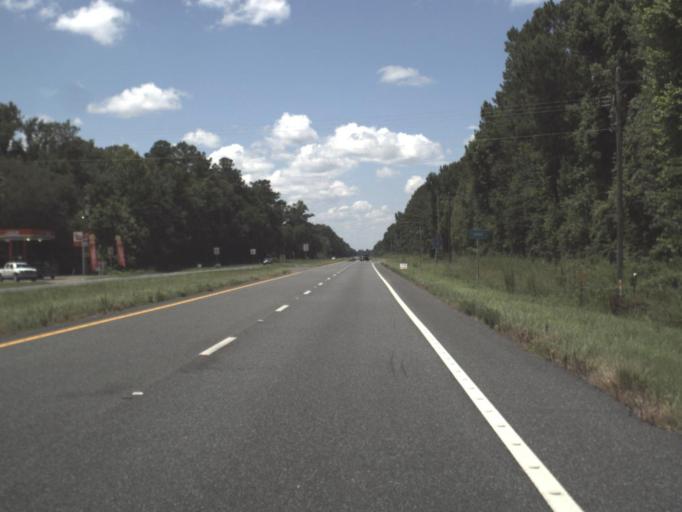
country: US
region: Florida
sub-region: Taylor County
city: Perry
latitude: 30.2995
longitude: -83.7446
